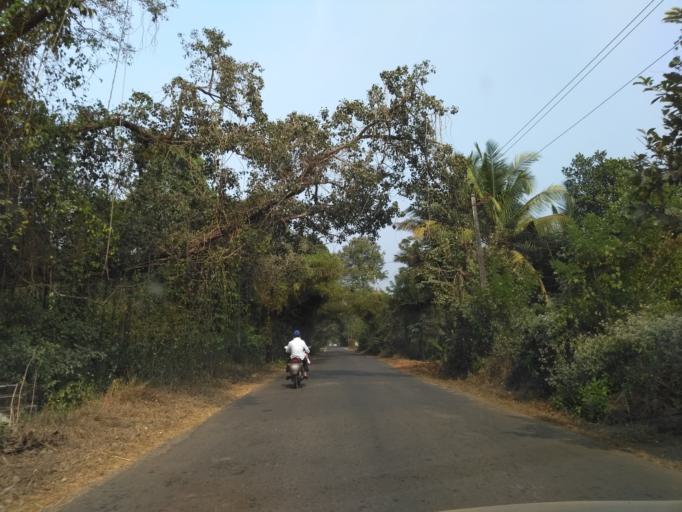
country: IN
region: Goa
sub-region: North Goa
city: Dicholi
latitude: 15.7221
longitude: 73.9528
